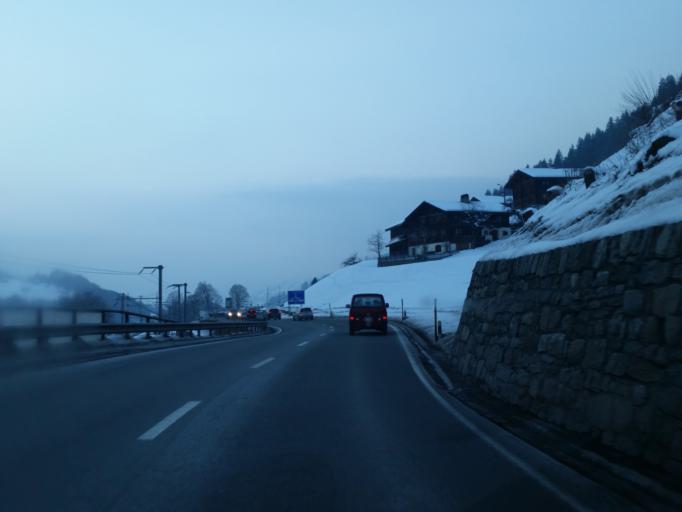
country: CH
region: Grisons
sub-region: Praettigau/Davos District
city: Klosters Serneus
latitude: 46.8927
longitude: 9.8462
